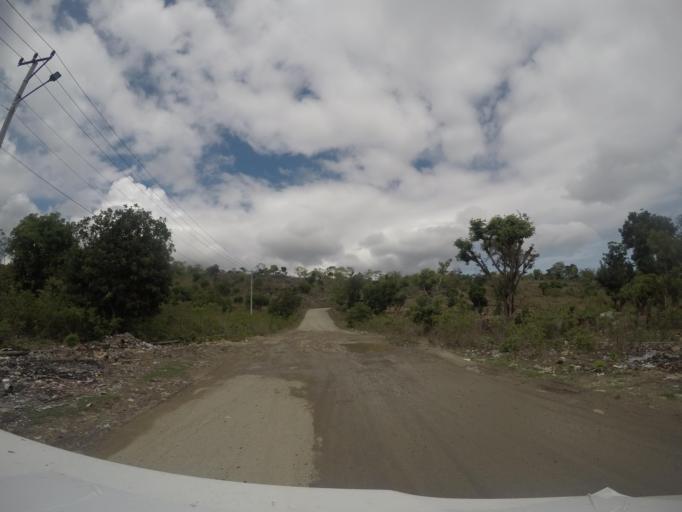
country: TL
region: Baucau
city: Baucau
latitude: -8.4699
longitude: 126.4352
